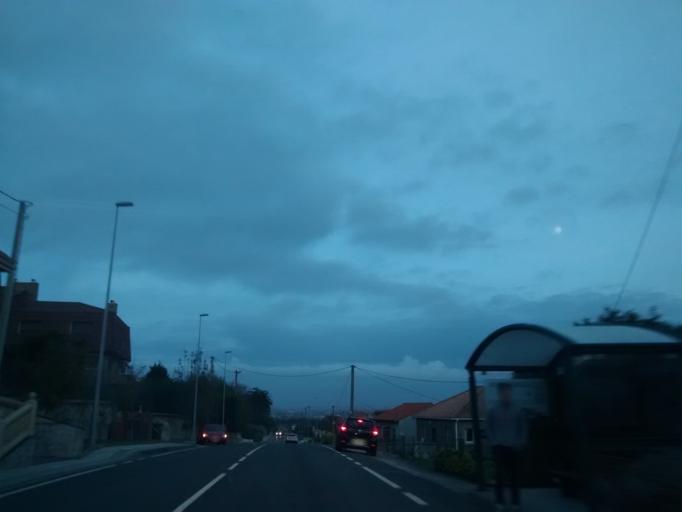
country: ES
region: Cantabria
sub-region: Provincia de Cantabria
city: Santa Cruz de Bezana
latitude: 43.4611
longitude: -3.9230
